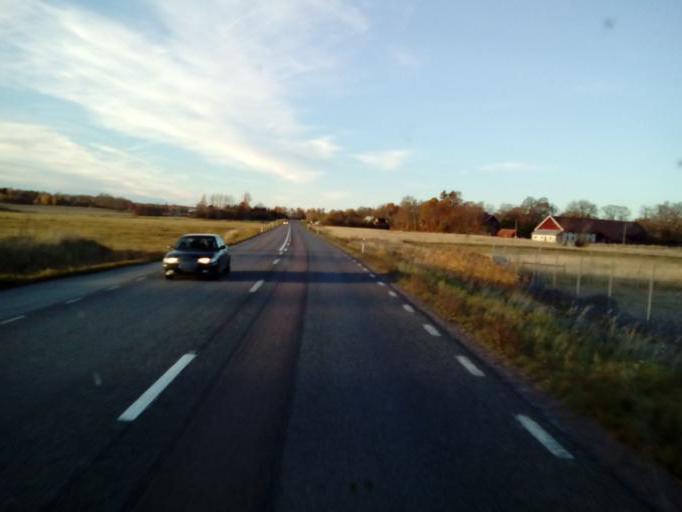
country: SE
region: OErebro
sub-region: Kumla Kommun
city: Hallabrottet
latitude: 59.1768
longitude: 15.2604
